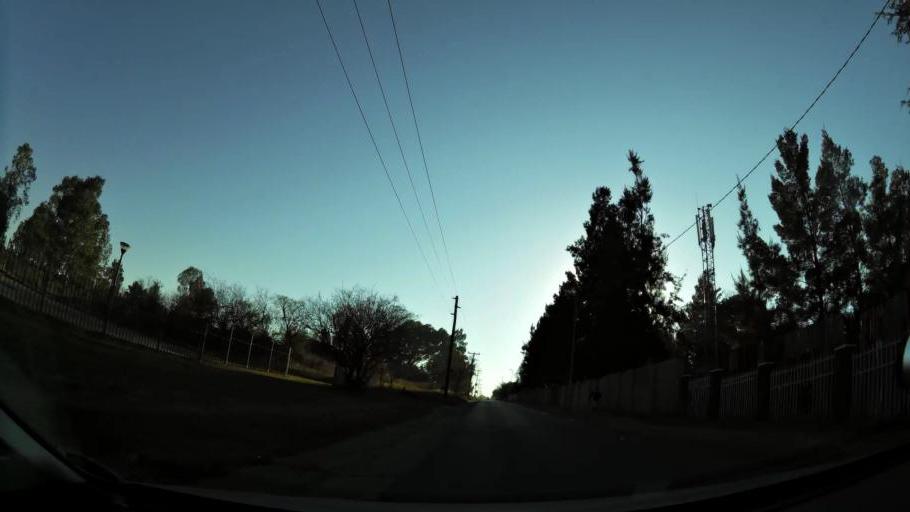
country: ZA
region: Gauteng
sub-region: City of Johannesburg Metropolitan Municipality
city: Midrand
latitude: -26.0188
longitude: 28.1352
